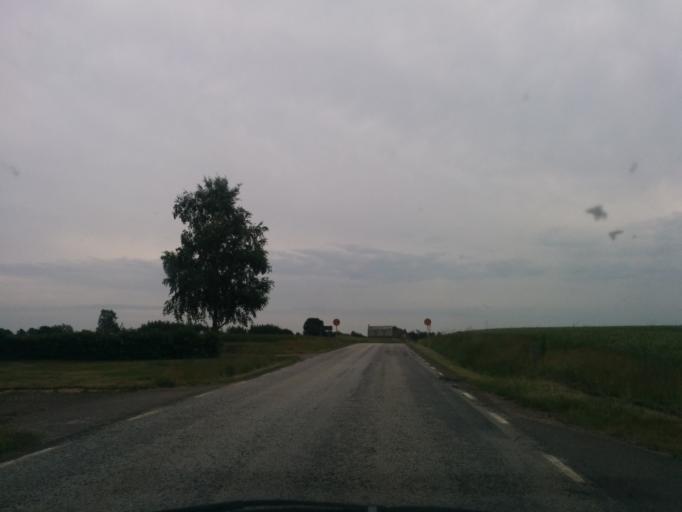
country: SE
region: Skane
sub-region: Lunds Kommun
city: Genarp
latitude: 55.6445
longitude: 13.3494
